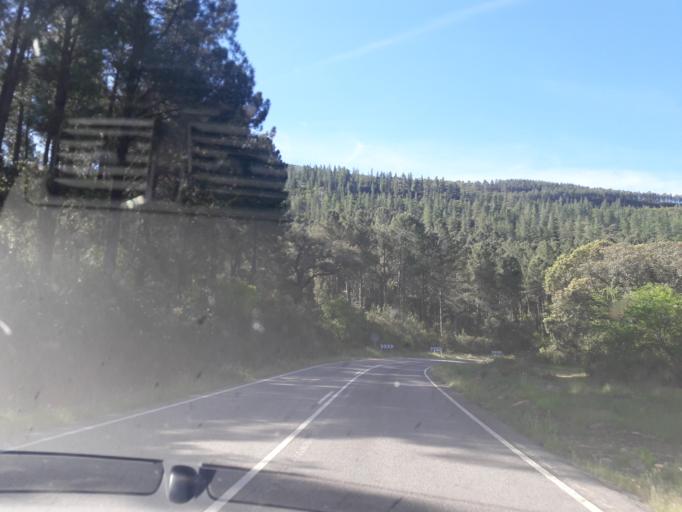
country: ES
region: Castille and Leon
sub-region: Provincia de Salamanca
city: Sotoserrano
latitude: 40.4071
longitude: -6.0523
